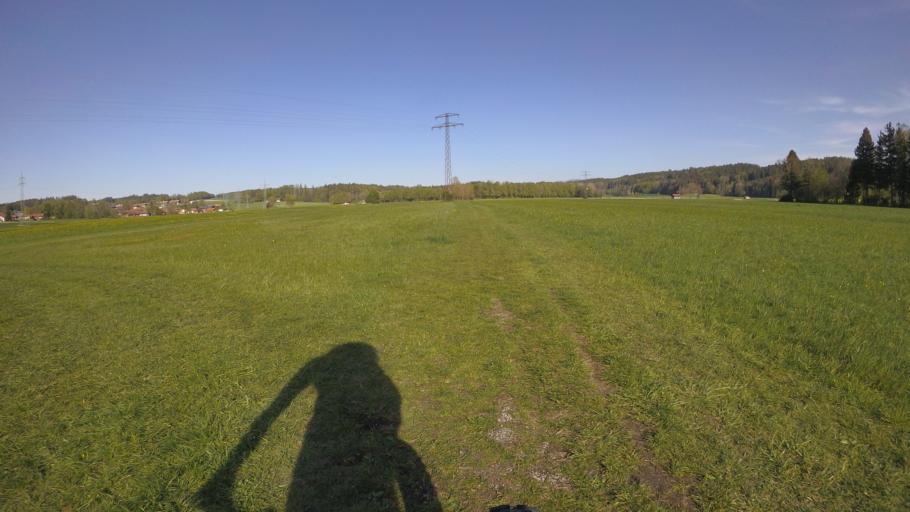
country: DE
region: Bavaria
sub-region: Upper Bavaria
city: Grabenstatt
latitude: 47.8468
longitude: 12.5530
